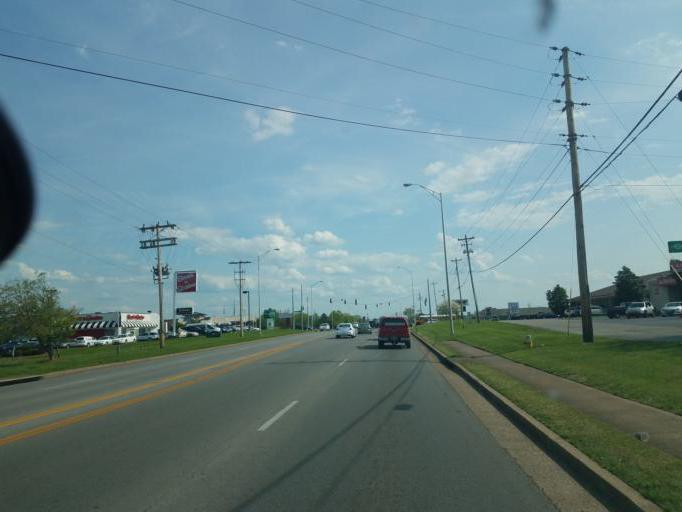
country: US
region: Kentucky
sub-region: Warren County
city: Bowling Green
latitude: 36.9710
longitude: -86.4347
